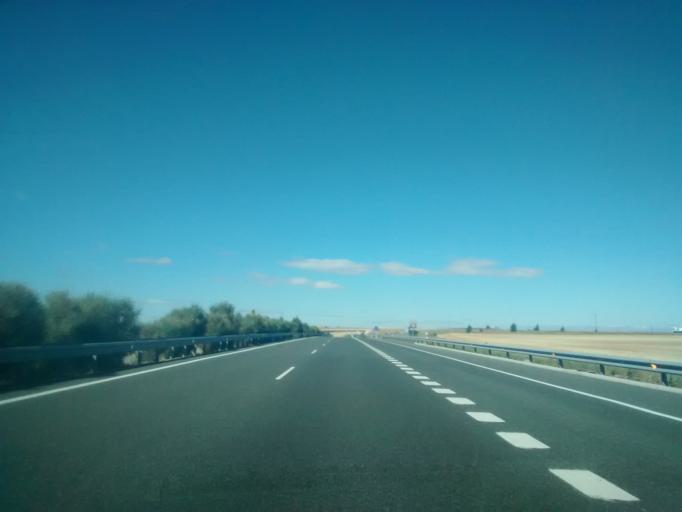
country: ES
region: Castille and Leon
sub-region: Provincia de Avila
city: Narros del Castillo
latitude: 40.8792
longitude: -5.0502
